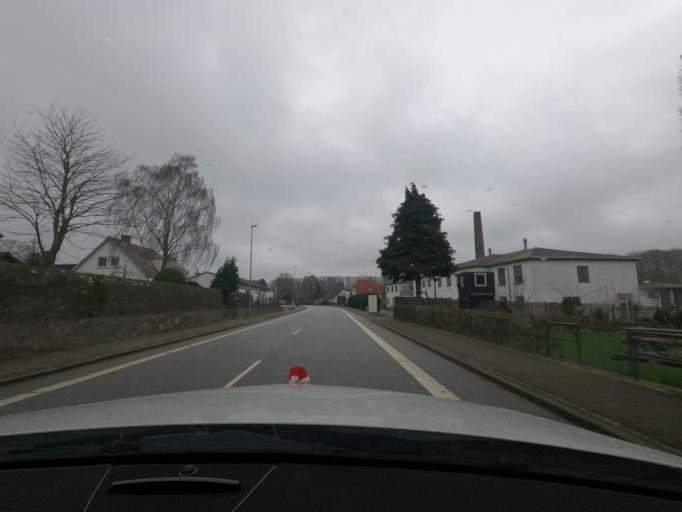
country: DK
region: South Denmark
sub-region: Haderslev Kommune
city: Starup
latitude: 55.2530
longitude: 9.6364
